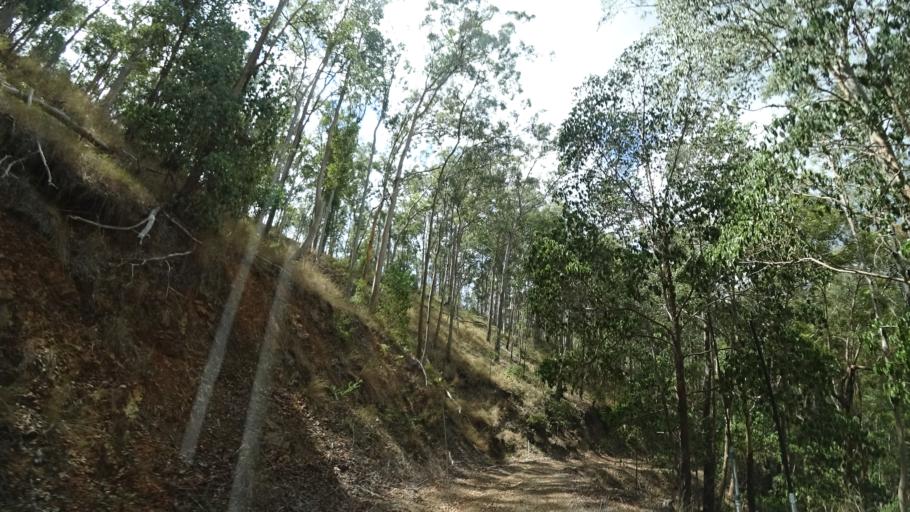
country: AU
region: Queensland
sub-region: Moreton Bay
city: Highvale
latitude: -27.3442
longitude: 152.7276
